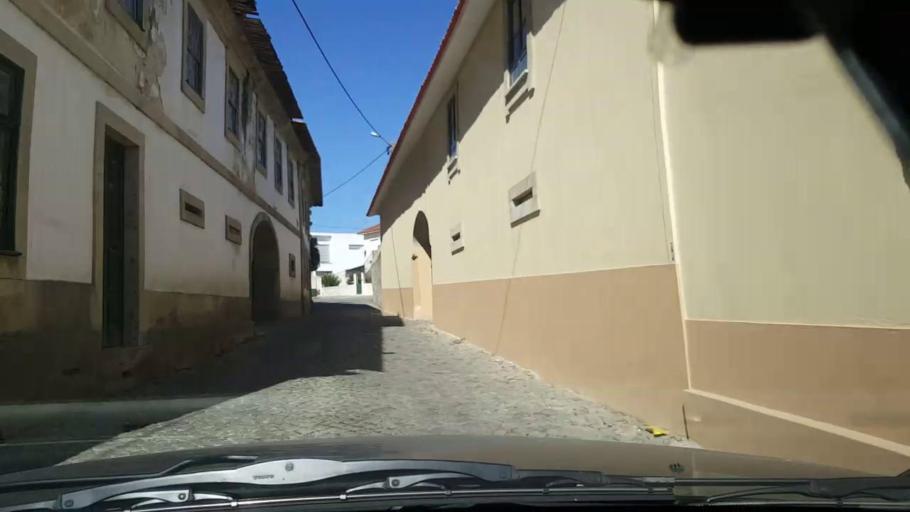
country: PT
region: Porto
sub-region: Maia
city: Gemunde
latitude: 41.3112
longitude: -8.6732
